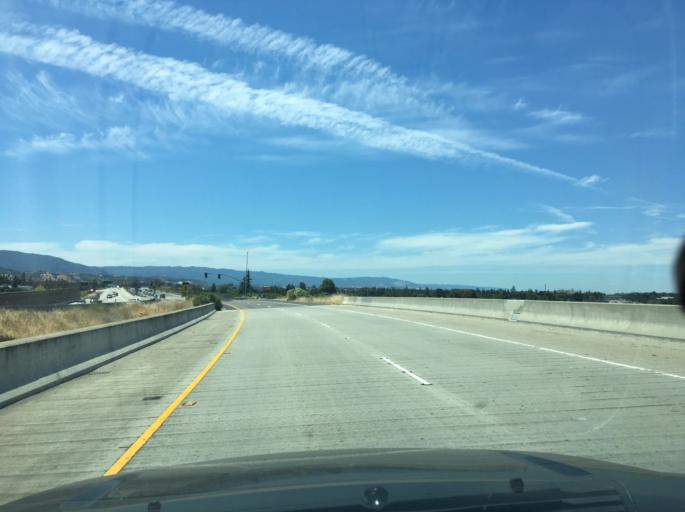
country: US
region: California
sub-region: Santa Clara County
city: Seven Trees
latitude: 37.2421
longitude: -121.7695
